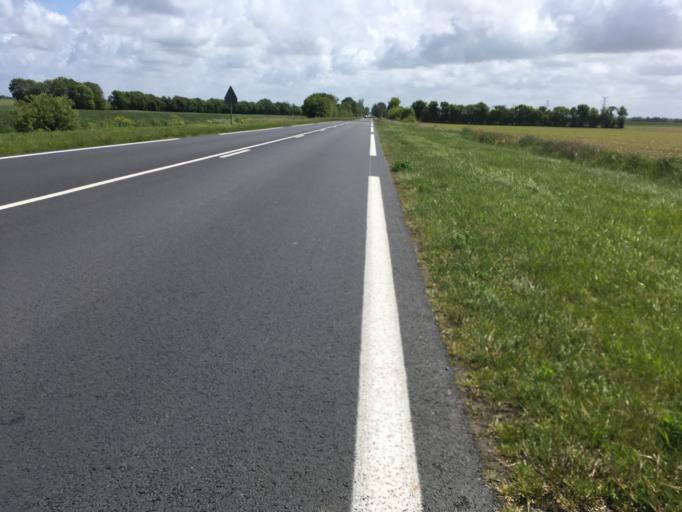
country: FR
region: Poitou-Charentes
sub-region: Departement de la Charente-Maritime
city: La Jarrie
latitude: 46.1051
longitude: -0.9754
